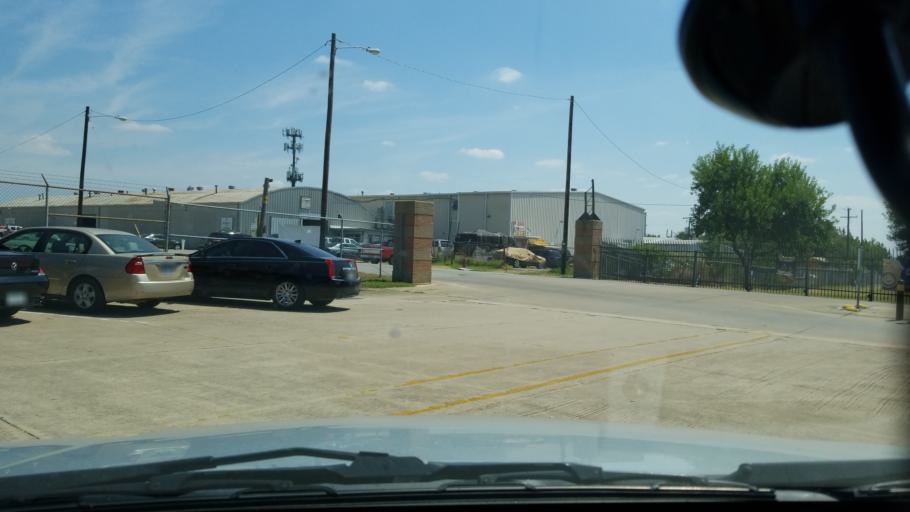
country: US
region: Texas
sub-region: Dallas County
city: Grand Prairie
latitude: 32.7419
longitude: -96.9583
